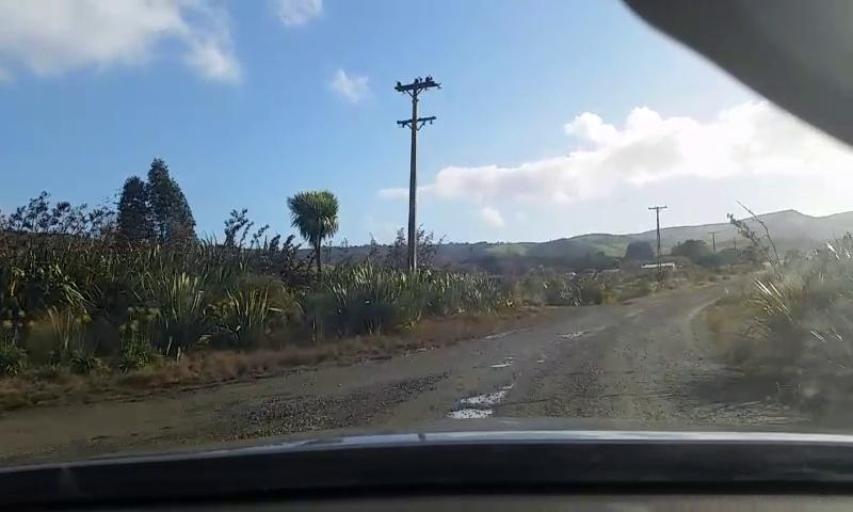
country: NZ
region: Otago
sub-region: Clutha District
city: Papatowai
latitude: -46.6280
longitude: 169.1367
